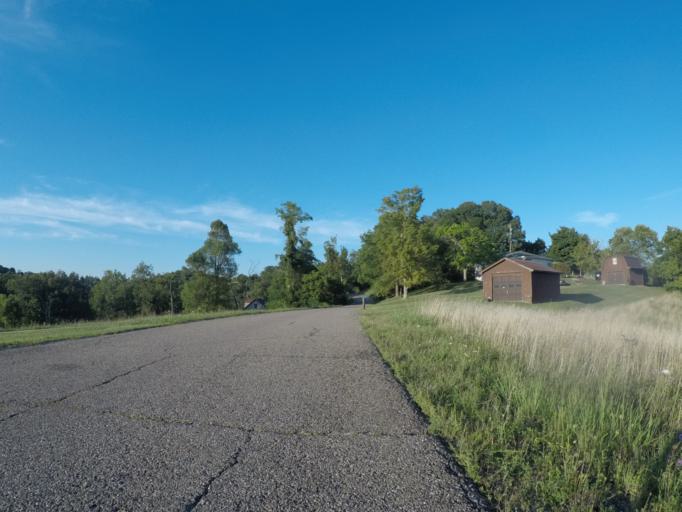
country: US
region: Ohio
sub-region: Lawrence County
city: Coal Grove
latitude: 38.5899
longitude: -82.5504
